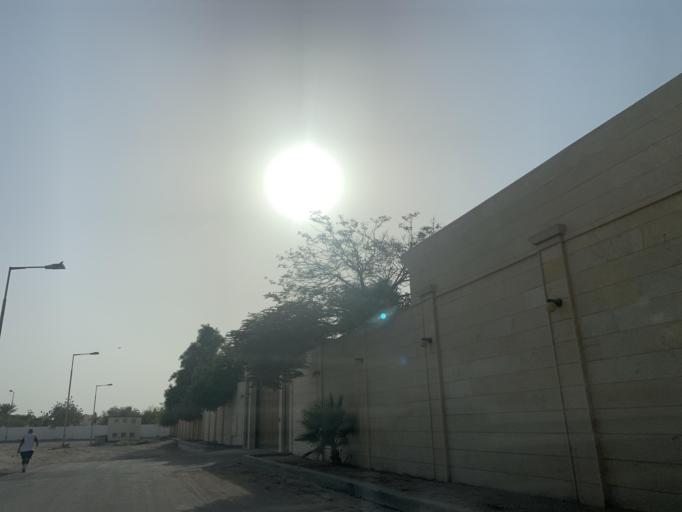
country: BH
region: Central Governorate
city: Madinat Hamad
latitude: 26.1757
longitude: 50.4751
